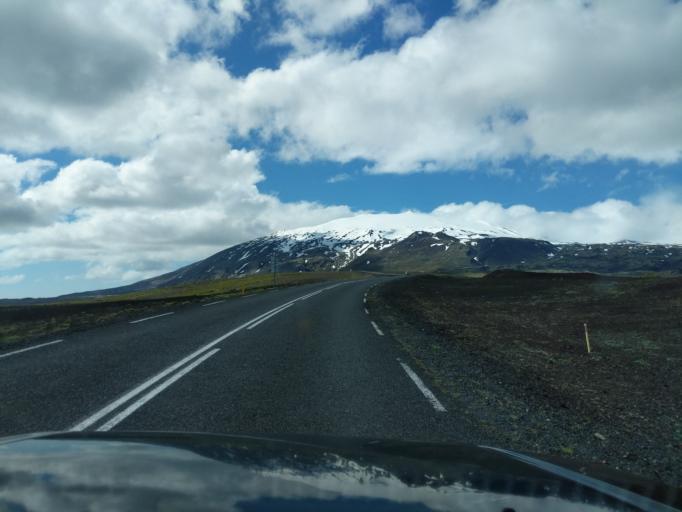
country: IS
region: West
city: Olafsvik
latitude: 64.7509
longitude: -23.6581
